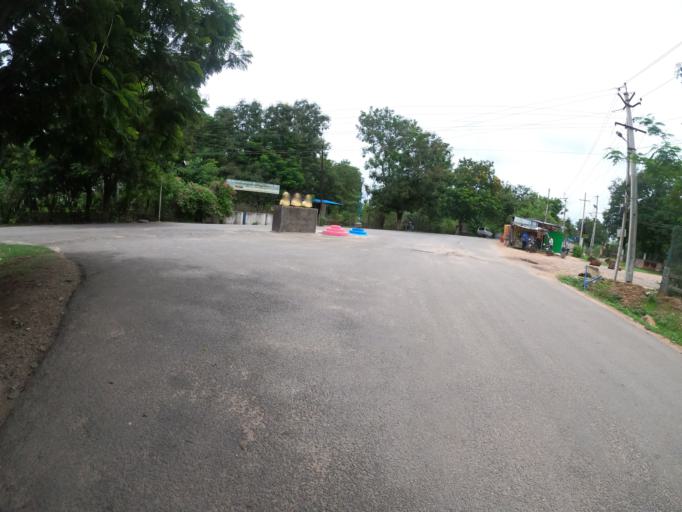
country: IN
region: Telangana
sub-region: Hyderabad
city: Hyderabad
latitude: 17.3397
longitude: 78.3615
